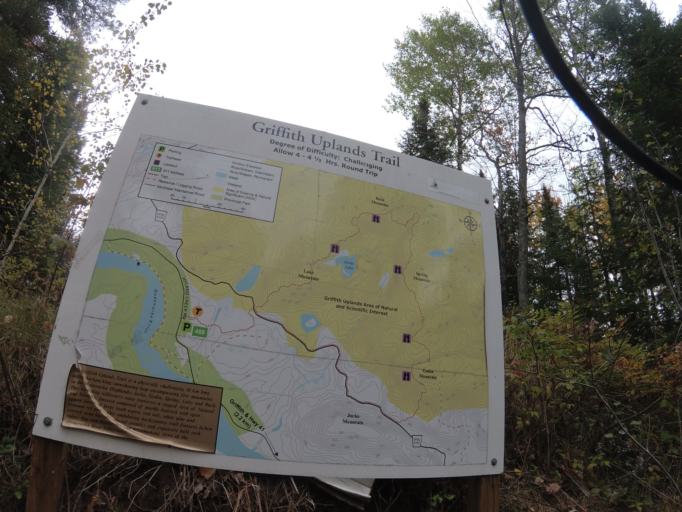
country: CA
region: Ontario
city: Renfrew
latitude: 45.2604
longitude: -77.2003
